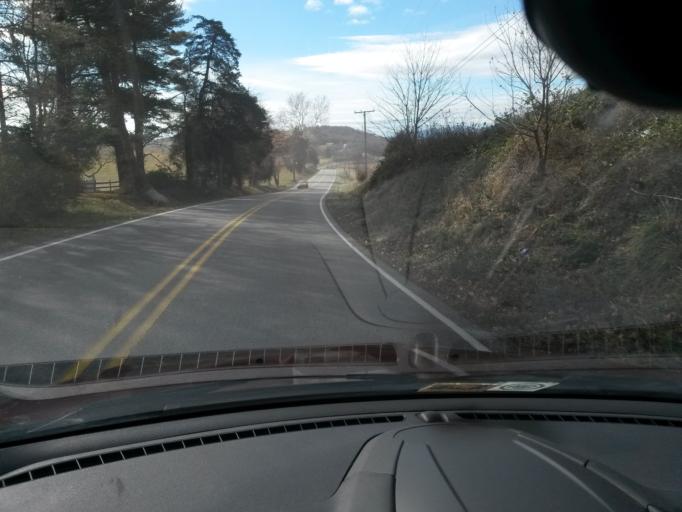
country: US
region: Virginia
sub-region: Rockingham County
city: Bridgewater
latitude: 38.3608
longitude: -79.0185
